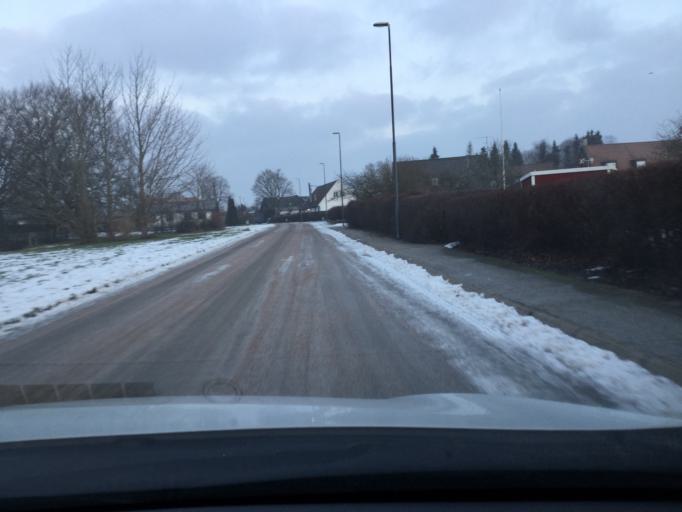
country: SE
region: Skane
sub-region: Hoors Kommun
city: Loberod
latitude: 55.7730
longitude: 13.5119
